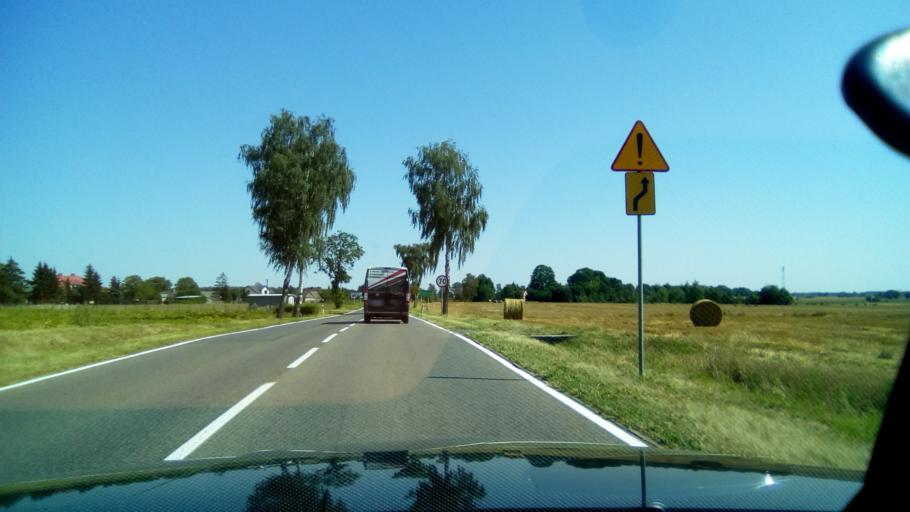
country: PL
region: Masovian Voivodeship
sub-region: Powiat plocki
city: Starozreby
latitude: 52.6176
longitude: 19.9417
